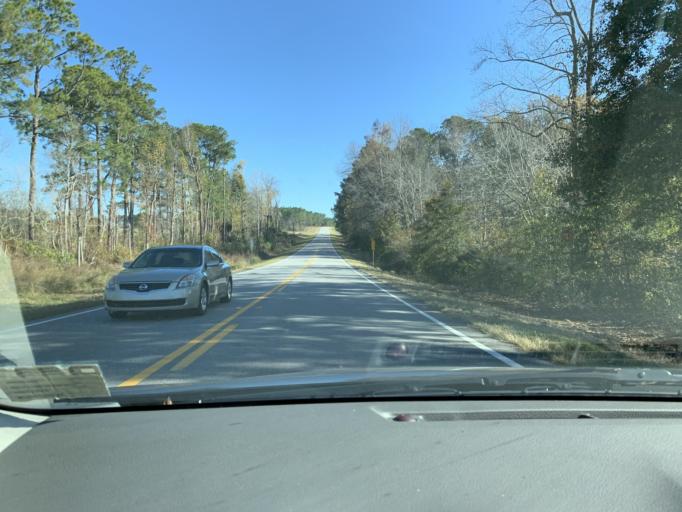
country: US
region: Georgia
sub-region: Ben Hill County
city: Fitzgerald
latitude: 31.7744
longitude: -83.0925
